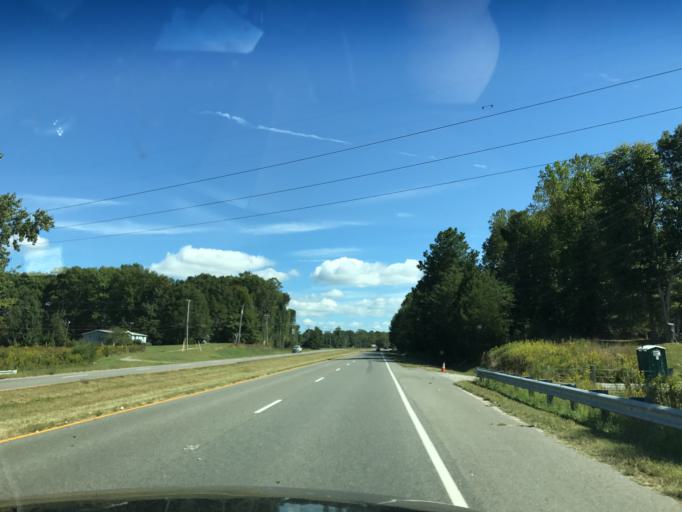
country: US
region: Virginia
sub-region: Essex County
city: Tappahannock
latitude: 37.8540
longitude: -76.8133
